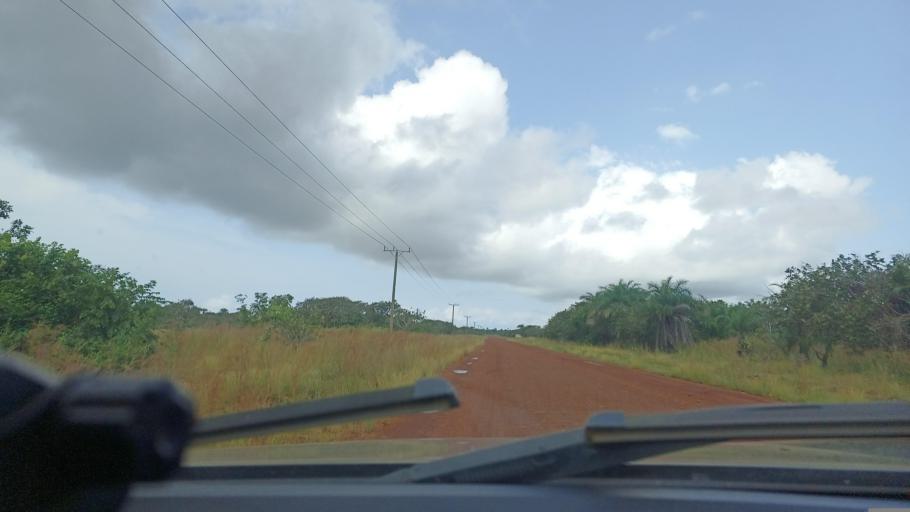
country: LR
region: Grand Cape Mount
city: Robertsport
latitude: 6.6916
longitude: -11.2718
